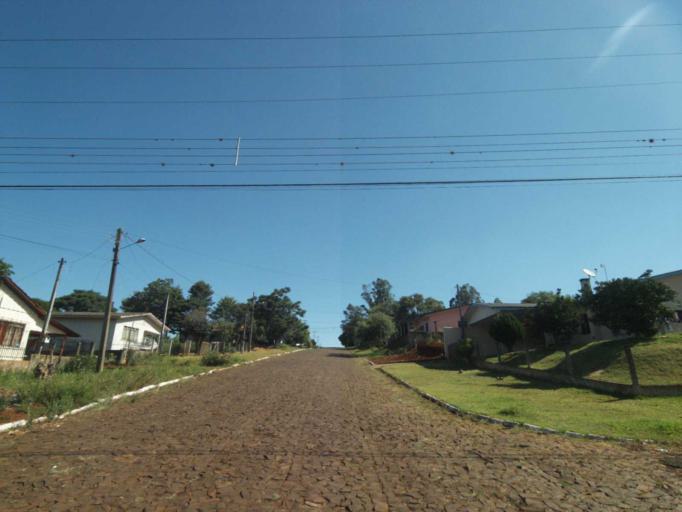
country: BR
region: Parana
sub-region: Laranjeiras Do Sul
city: Laranjeiras do Sul
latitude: -25.3803
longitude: -52.2000
